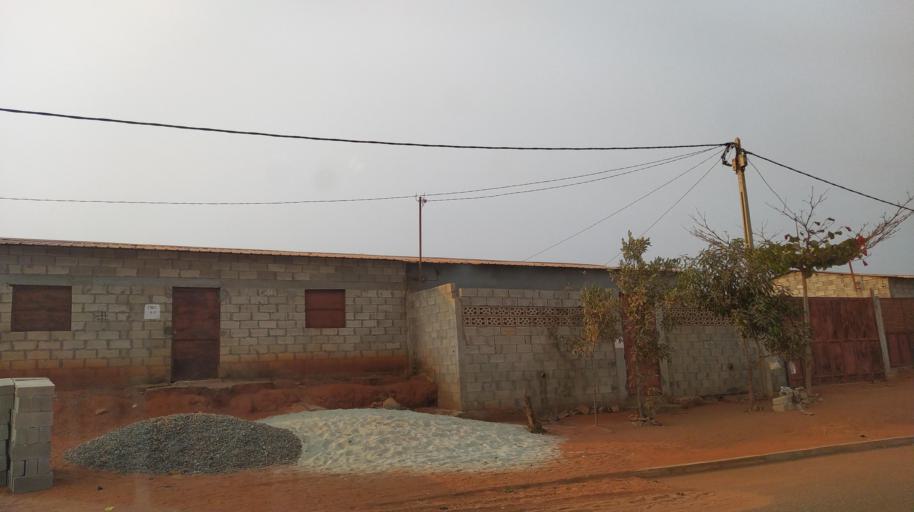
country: AO
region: Luanda
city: Luanda
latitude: -9.0713
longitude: 13.4262
